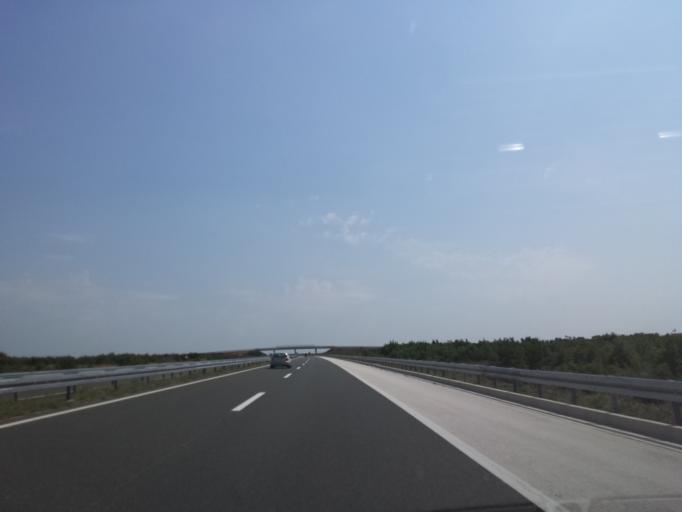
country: HR
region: Sibensko-Kniniska
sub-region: Grad Sibenik
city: Pirovac
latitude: 43.9296
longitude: 15.7174
